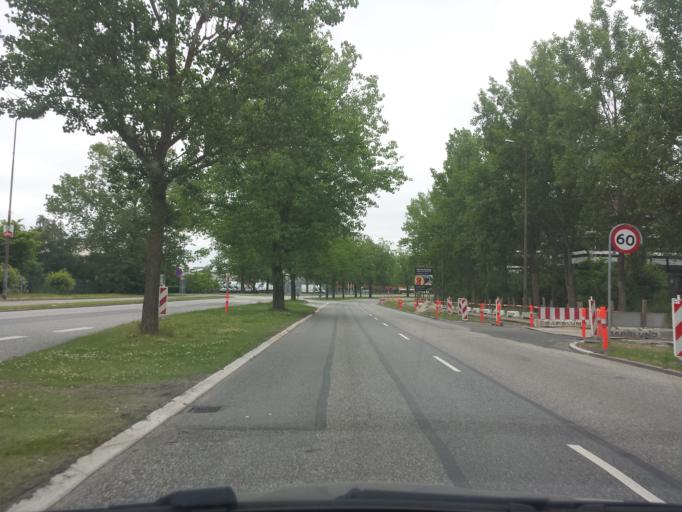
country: DK
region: Capital Region
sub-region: Herlev Kommune
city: Herlev
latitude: 55.6998
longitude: 12.4193
